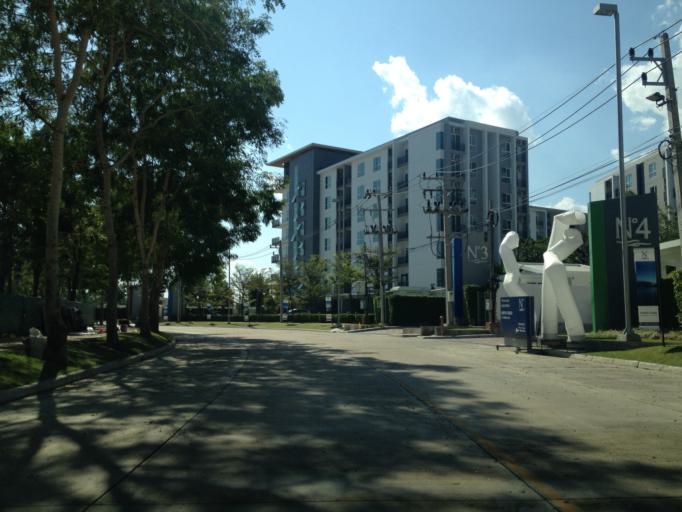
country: TH
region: Chiang Mai
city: Chiang Mai
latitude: 18.7601
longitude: 98.9509
